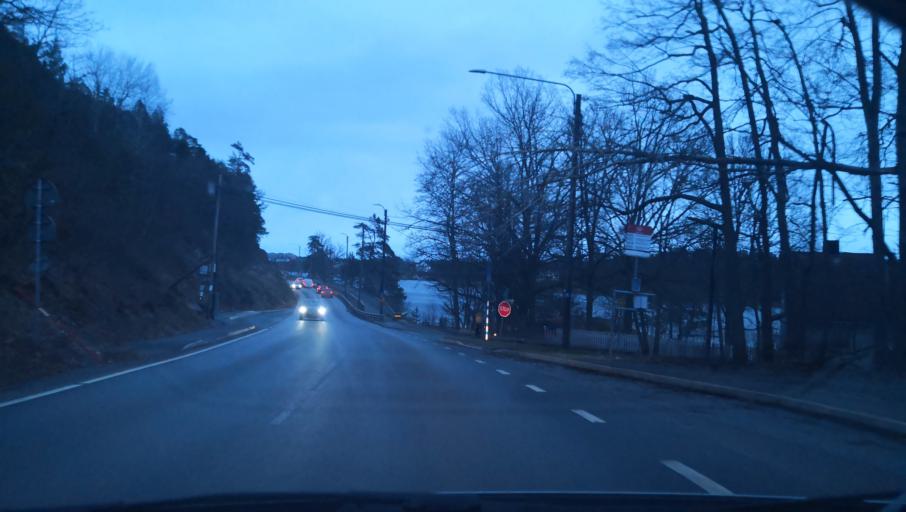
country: SE
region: Stockholm
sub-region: Varmdo Kommun
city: Gustavsberg
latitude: 59.3277
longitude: 18.3556
